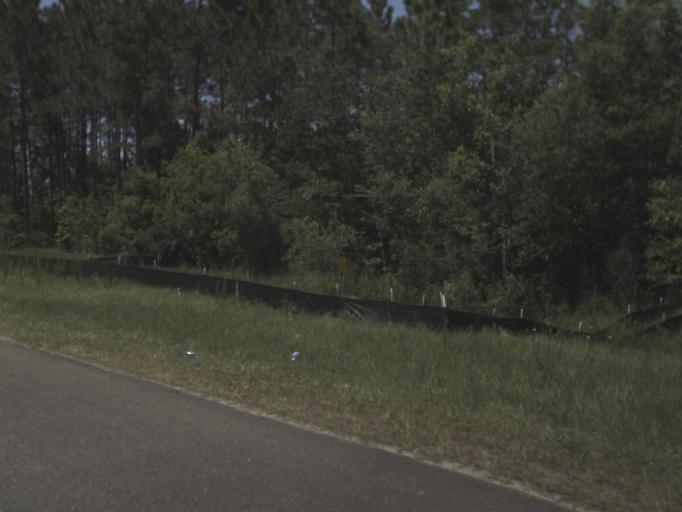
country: US
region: Florida
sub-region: Clay County
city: Bellair-Meadowbrook Terrace
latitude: 30.2256
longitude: -81.8415
